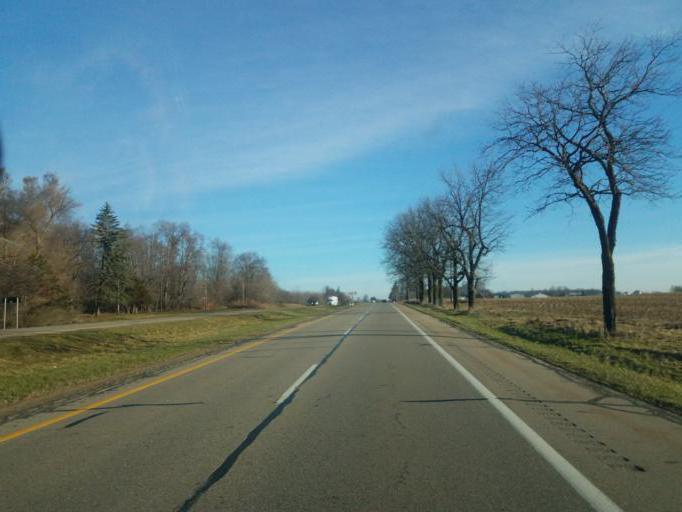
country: US
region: Michigan
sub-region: Clinton County
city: Saint Johns
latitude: 43.0535
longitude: -84.5638
